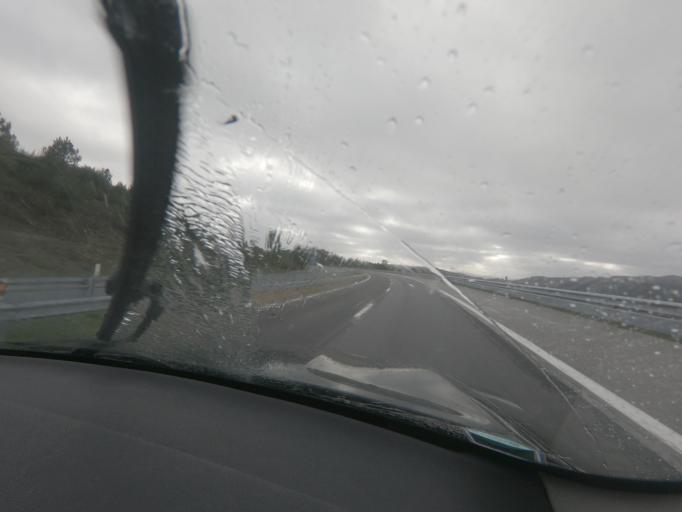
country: PT
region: Viseu
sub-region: Castro Daire
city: Castro Daire
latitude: 40.8339
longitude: -7.9375
